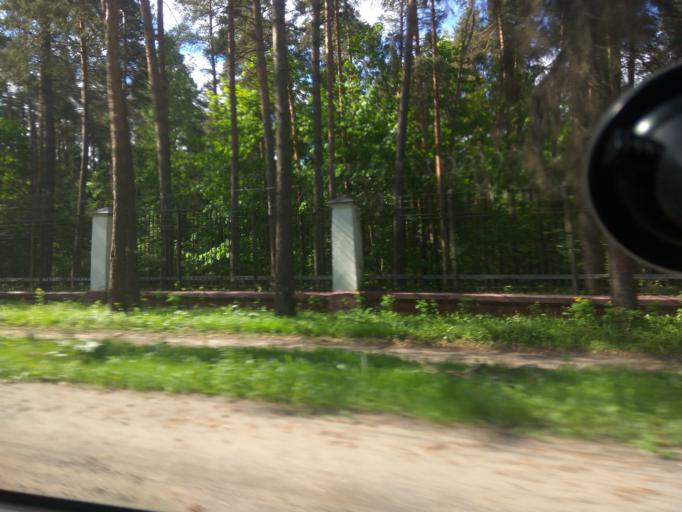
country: RU
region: Moskovskaya
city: Kratovo
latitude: 55.5775
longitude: 38.1596
